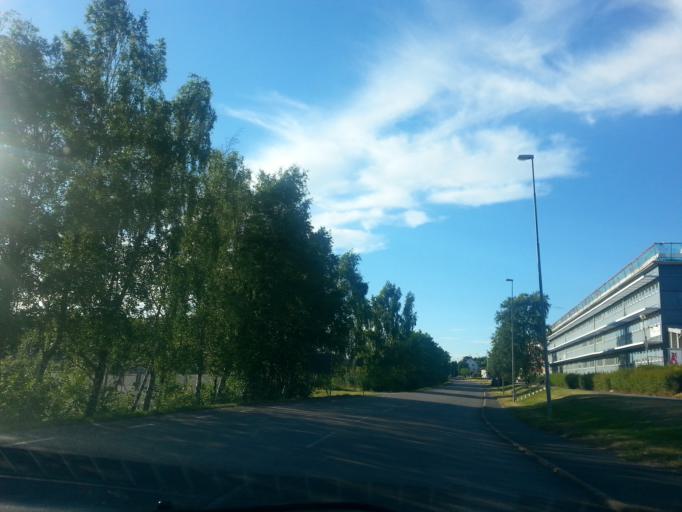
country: SE
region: Vaestra Goetaland
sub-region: Molndal
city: Moelndal
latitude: 57.6575
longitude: 12.0198
